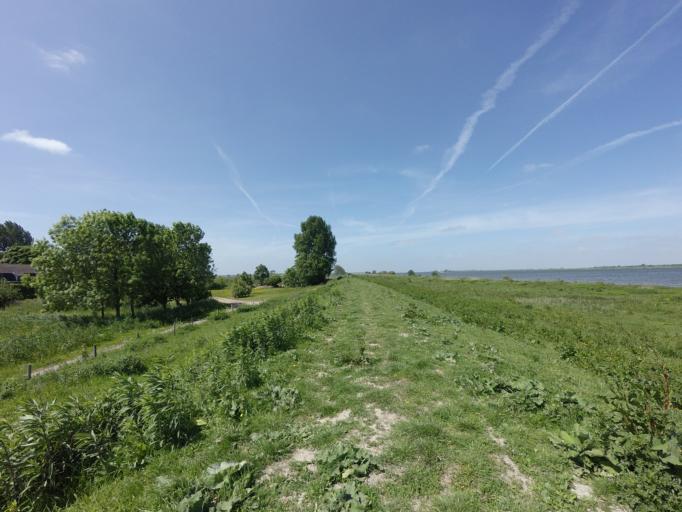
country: NL
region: South Holland
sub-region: Gemeente Spijkenisse
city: Spijkenisse
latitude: 51.7496
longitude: 4.2936
